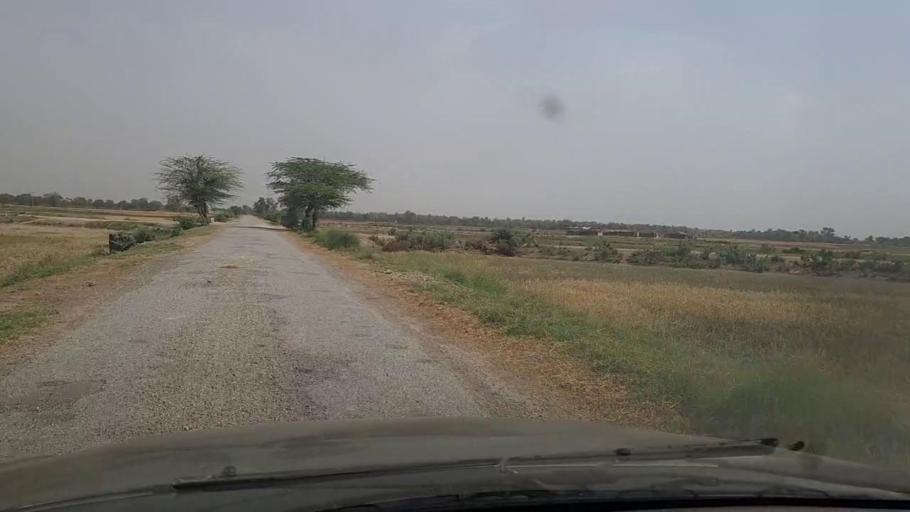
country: PK
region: Sindh
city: Lakhi
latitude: 27.8491
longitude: 68.7536
